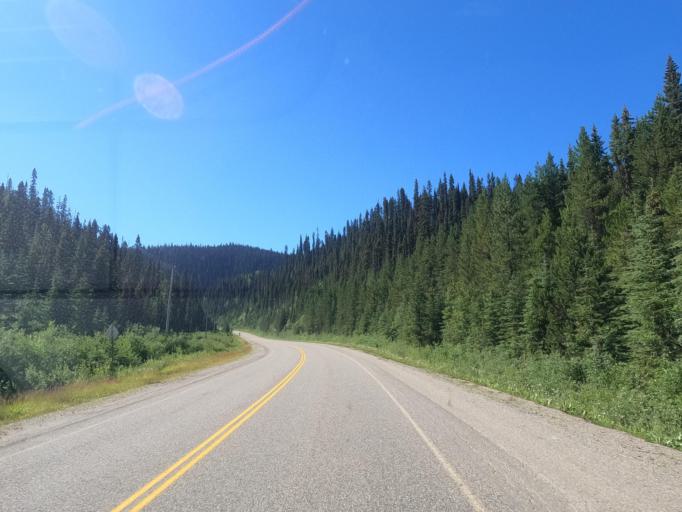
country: CA
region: British Columbia
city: Quesnel
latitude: 53.0834
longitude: -121.6750
